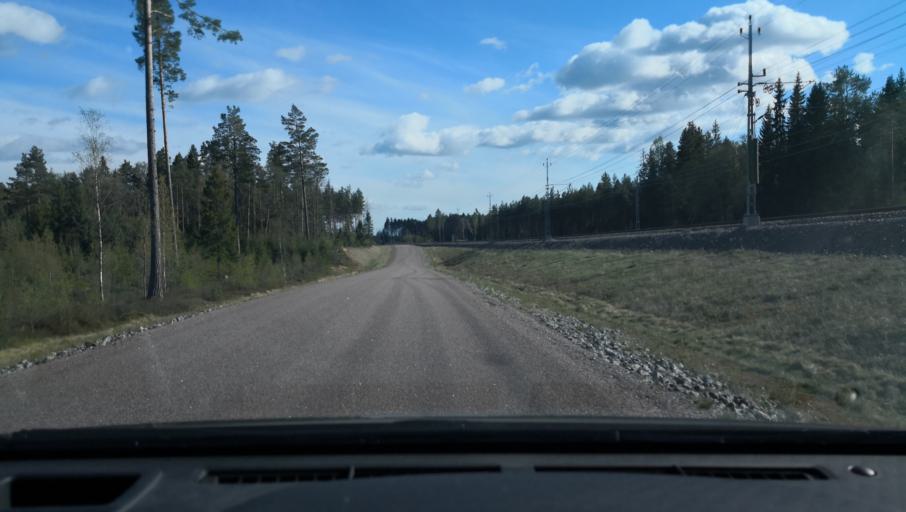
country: SE
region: OErebro
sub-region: Askersunds Kommun
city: Asbro
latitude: 58.9424
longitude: 15.0408
